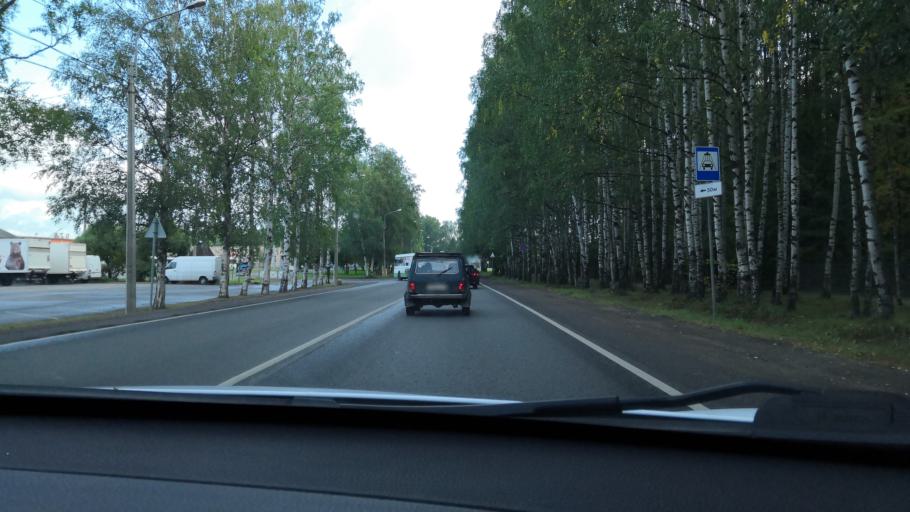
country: RU
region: St.-Petersburg
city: Pavlovsk
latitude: 59.6962
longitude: 30.4394
